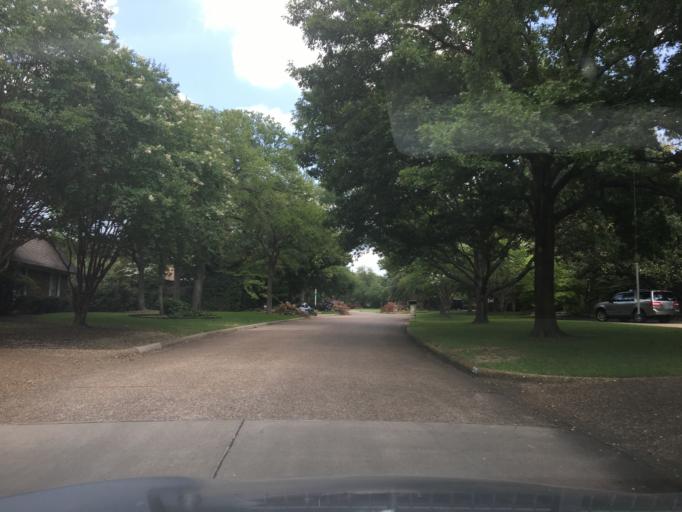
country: US
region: Texas
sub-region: Dallas County
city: University Park
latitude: 32.9005
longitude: -96.8185
